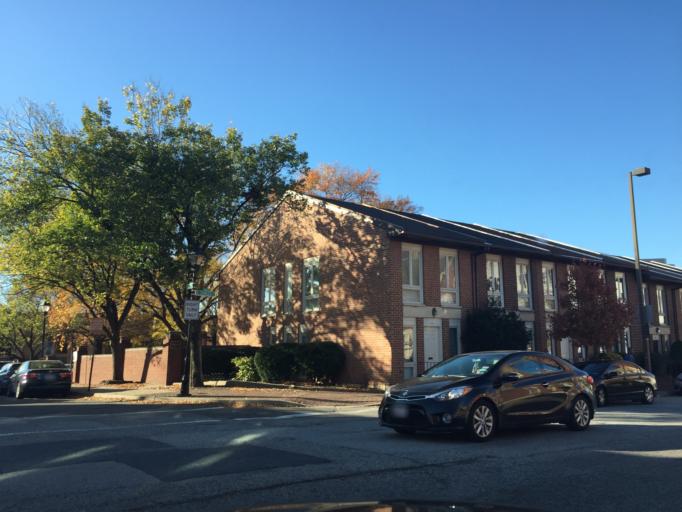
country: US
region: Maryland
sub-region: City of Baltimore
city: Baltimore
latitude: 39.2804
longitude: -76.6145
